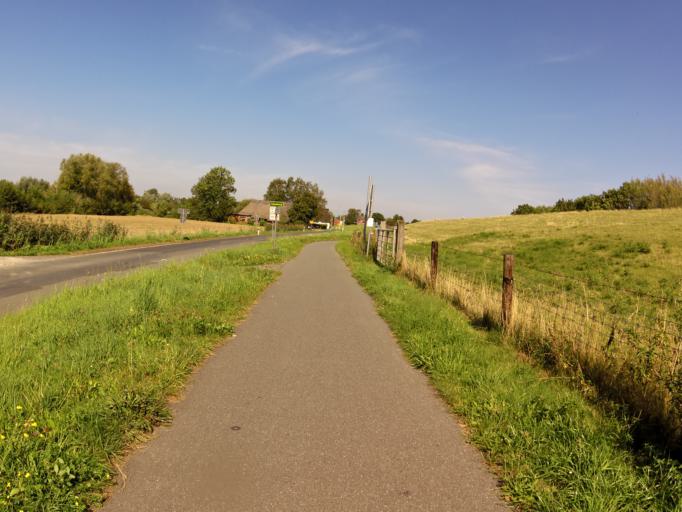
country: DE
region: Lower Saxony
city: Brake (Unterweser)
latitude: 53.2856
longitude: 8.4817
